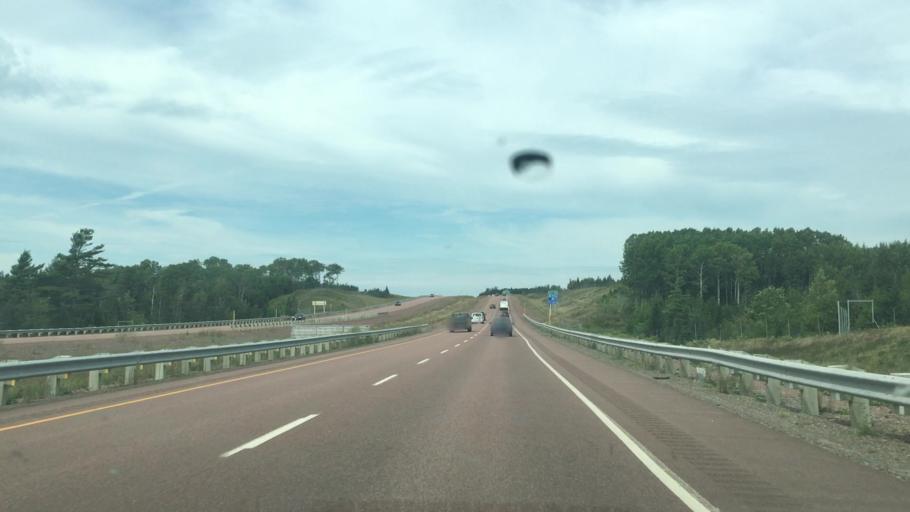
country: CA
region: Nova Scotia
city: Antigonish
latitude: 45.6031
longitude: -61.9514
